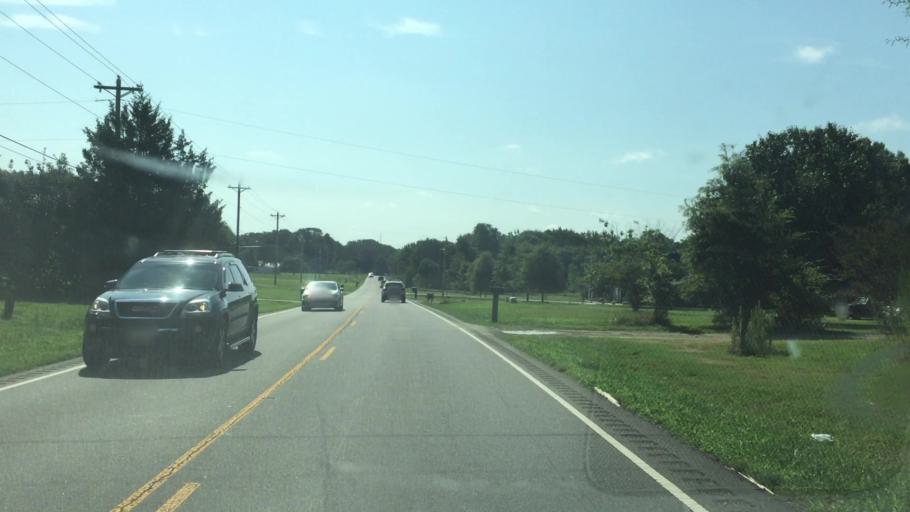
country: US
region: North Carolina
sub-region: Union County
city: Fairview
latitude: 35.1530
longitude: -80.5585
